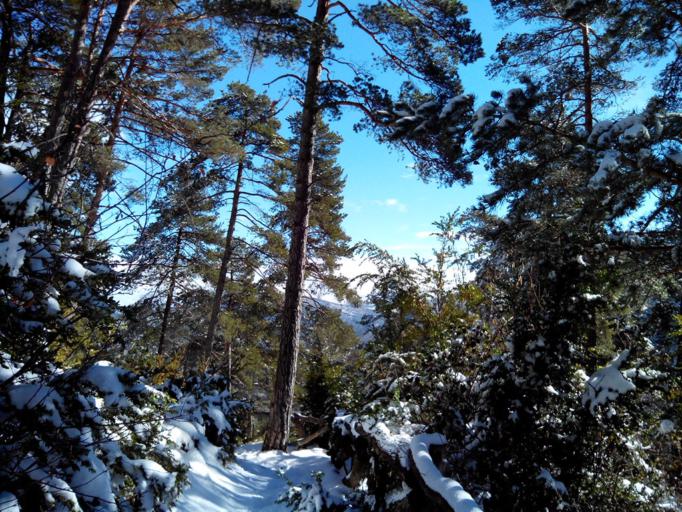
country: ES
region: Catalonia
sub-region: Provincia de Barcelona
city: Sant Julia de Cerdanyola
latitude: 42.2222
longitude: 1.9648
